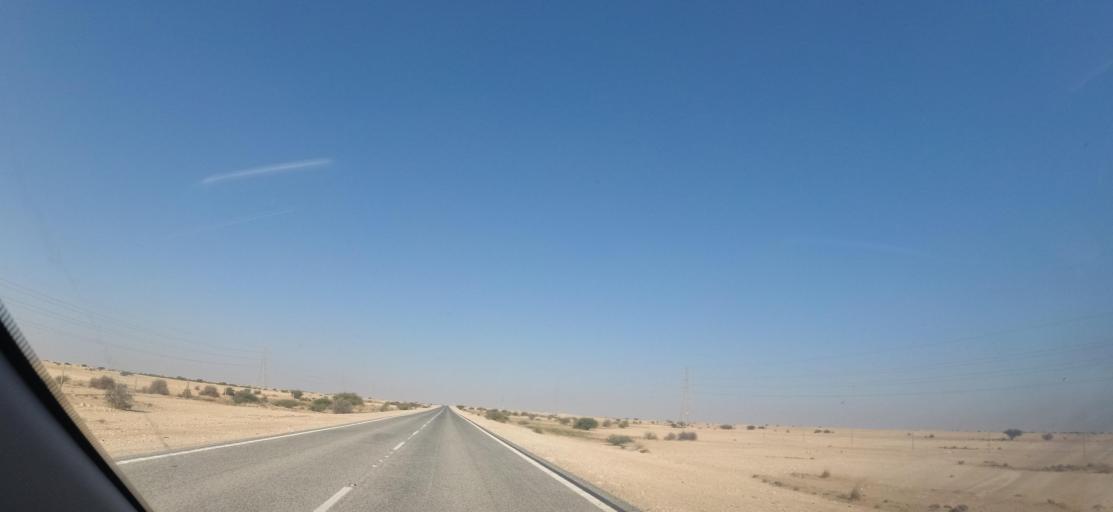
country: QA
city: Al Jumayliyah
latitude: 25.6452
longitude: 51.1073
